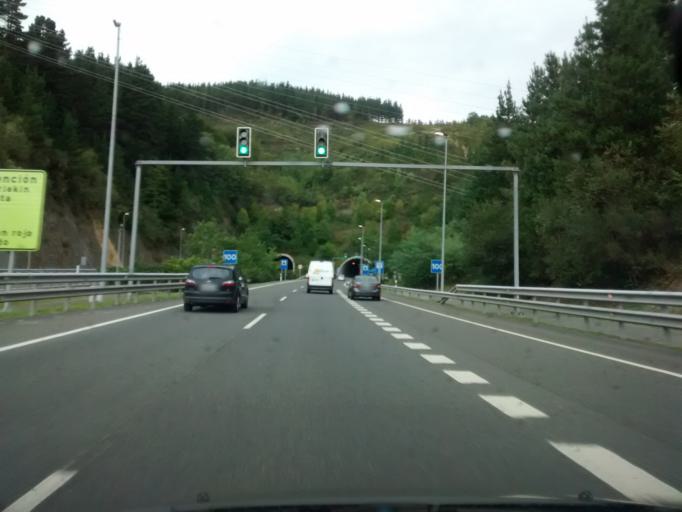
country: ES
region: Basque Country
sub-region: Provincia de Guipuzcoa
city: Bergara
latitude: 43.1333
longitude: -2.4252
